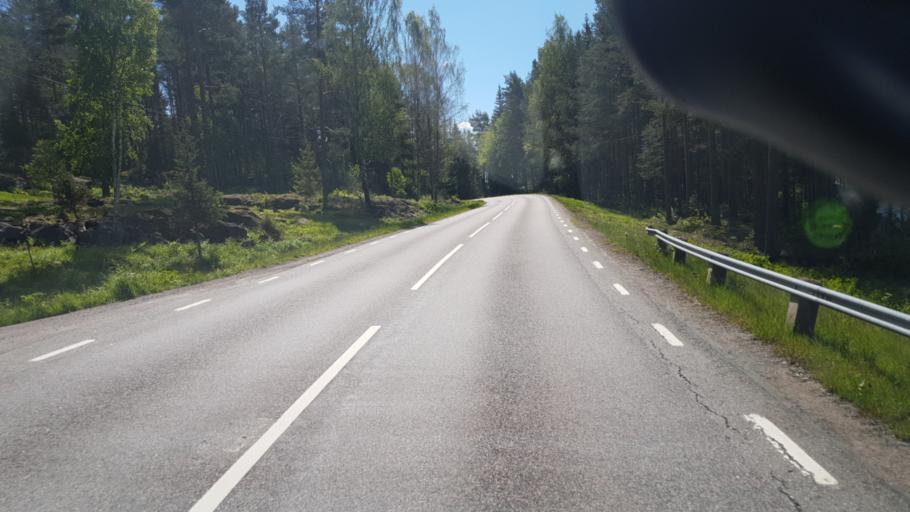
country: SE
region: Vaermland
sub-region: Grums Kommun
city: Slottsbron
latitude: 59.4518
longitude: 12.8961
